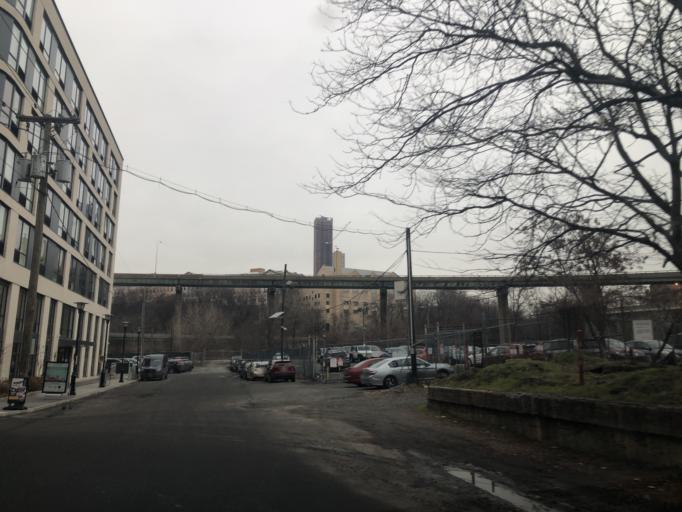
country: US
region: New Jersey
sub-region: Hudson County
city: Hoboken
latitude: 40.7295
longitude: -74.0497
